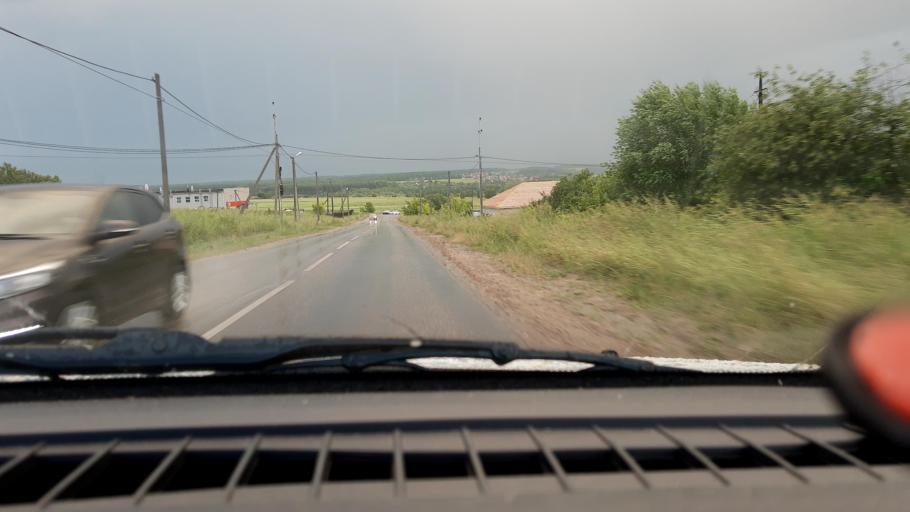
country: RU
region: Nizjnij Novgorod
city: Burevestnik
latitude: 56.0607
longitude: 43.8645
